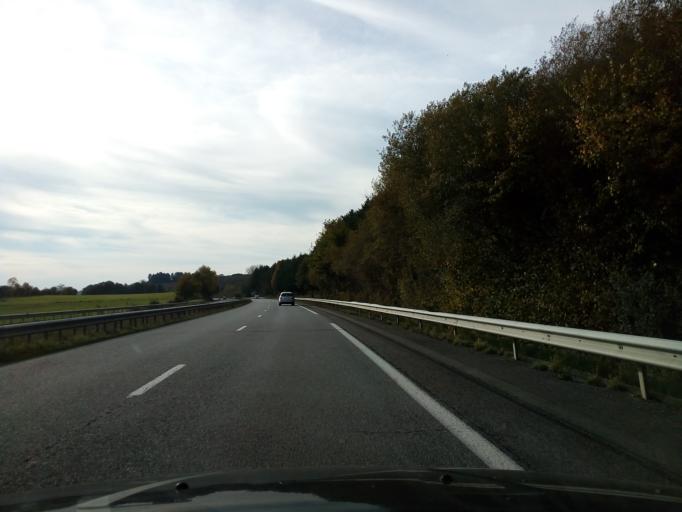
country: FR
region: Limousin
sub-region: Departement de la Creuse
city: La Souterraine
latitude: 46.2385
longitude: 1.5241
